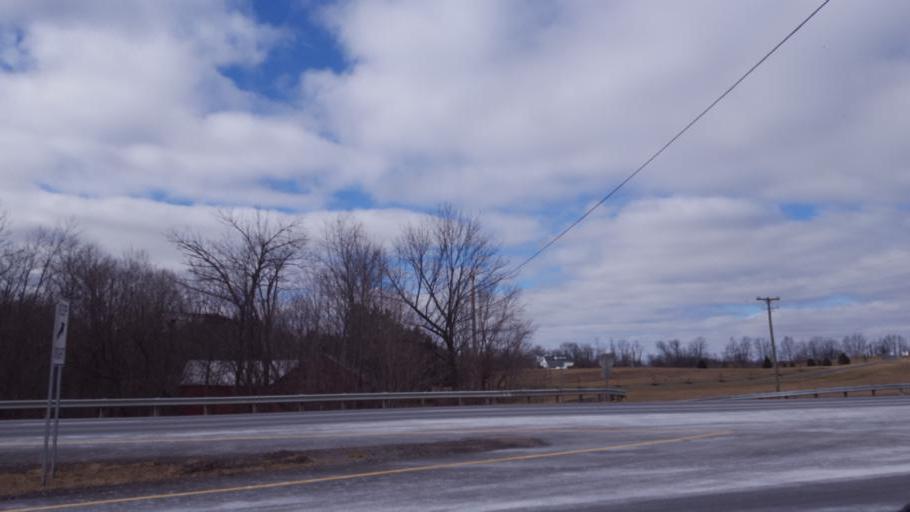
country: US
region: Ohio
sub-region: Sandusky County
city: Bellville
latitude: 40.6630
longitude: -82.5156
